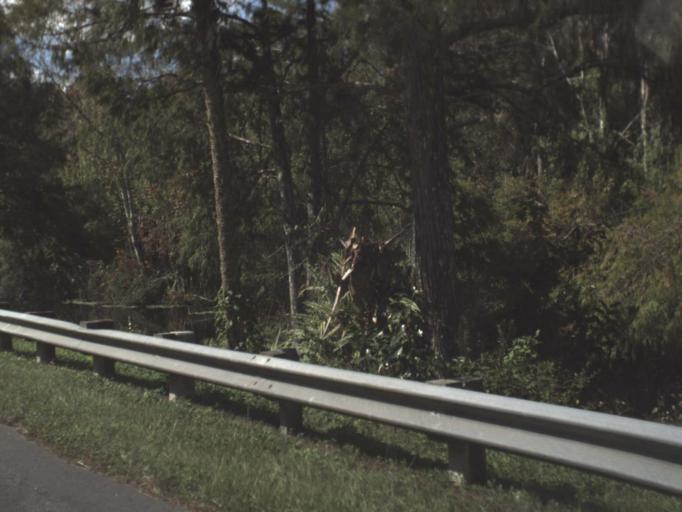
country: US
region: Florida
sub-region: Collier County
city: Marco
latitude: 25.8765
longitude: -81.2262
